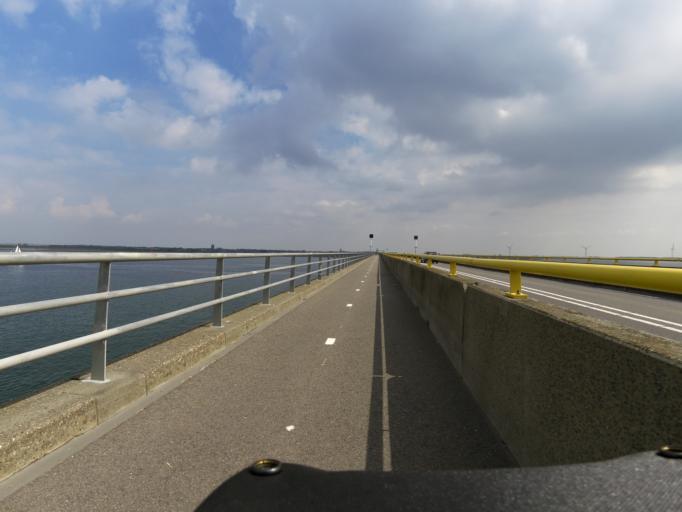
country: NL
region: Zeeland
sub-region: Gemeente Goes
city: Goes
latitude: 51.6219
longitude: 3.9041
